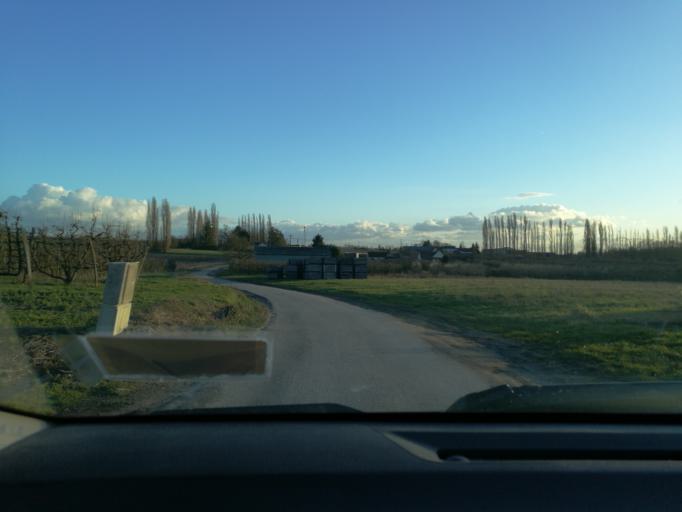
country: FR
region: Centre
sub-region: Departement du Loiret
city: Semoy
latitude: 47.9348
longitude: 1.9698
